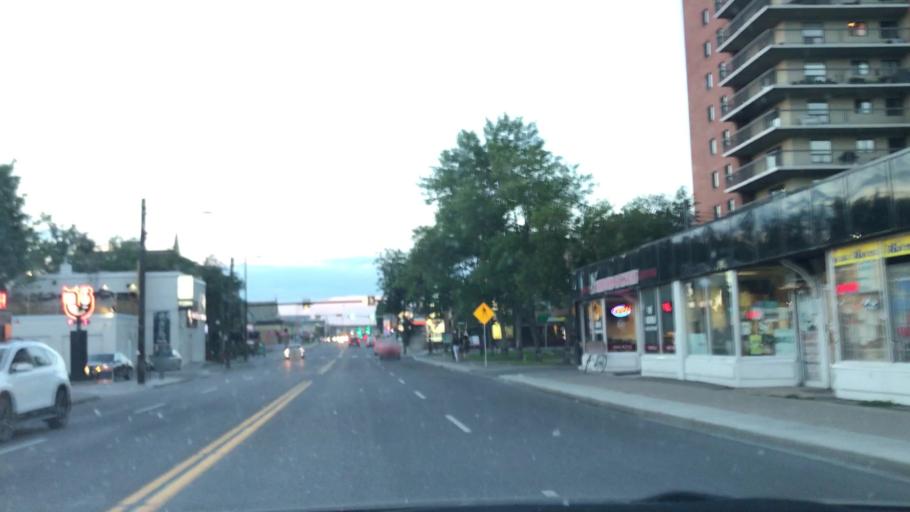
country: CA
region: Alberta
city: Calgary
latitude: 51.0386
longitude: -114.0947
